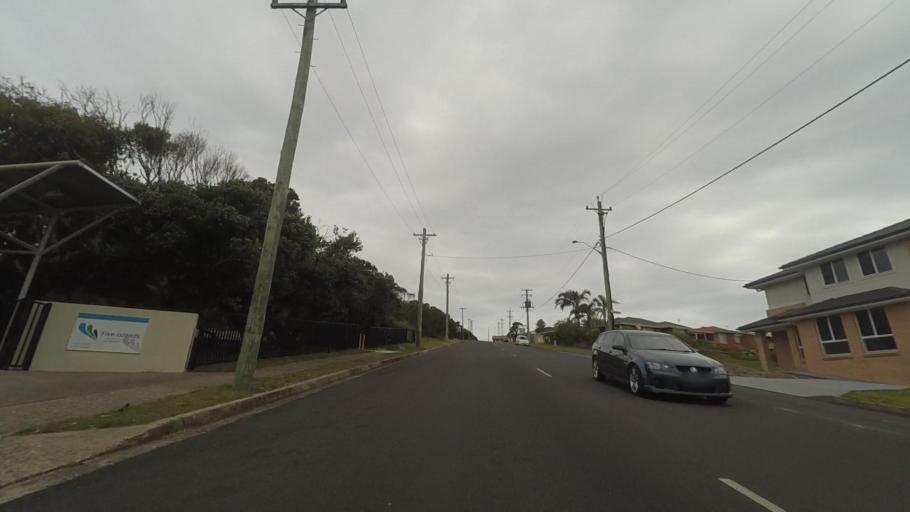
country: AU
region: New South Wales
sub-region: Wollongong
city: Port Kembla
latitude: -34.4904
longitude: 150.9129
